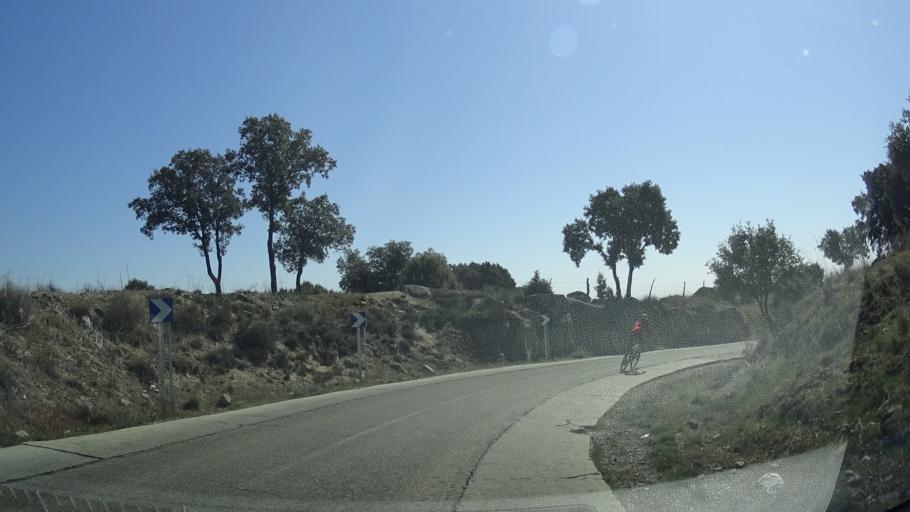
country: ES
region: Madrid
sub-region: Provincia de Madrid
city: Colmenar Viejo
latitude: 40.6442
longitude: -3.8142
